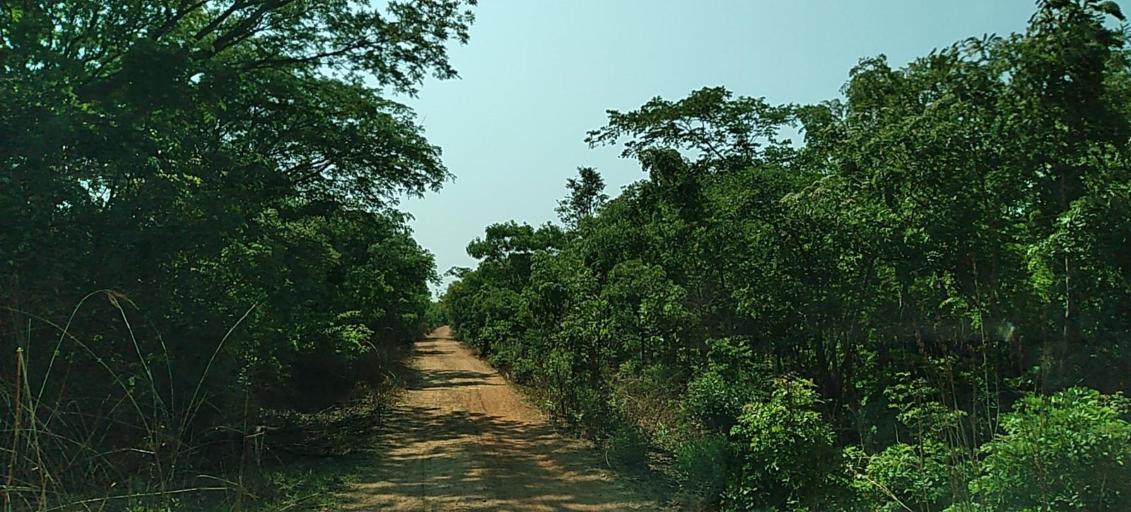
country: ZM
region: Copperbelt
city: Luanshya
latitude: -13.2778
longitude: 28.3073
